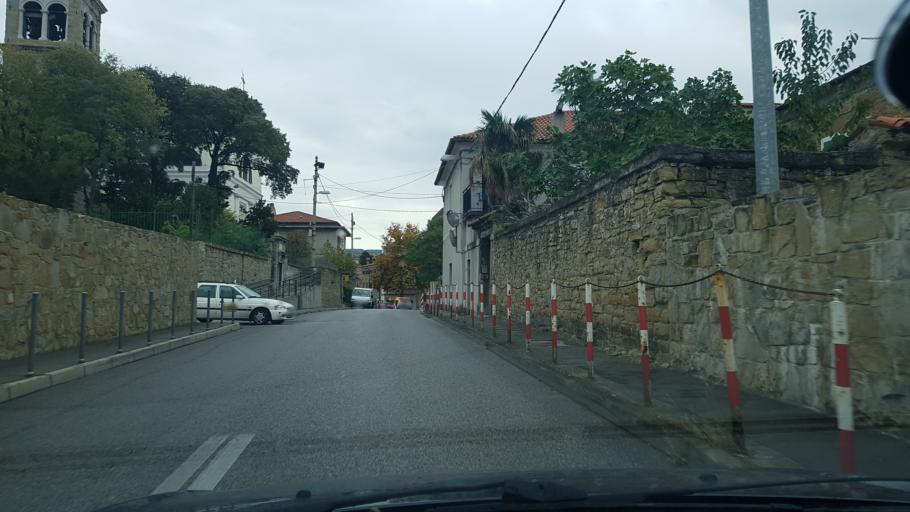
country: IT
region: Friuli Venezia Giulia
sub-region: Provincia di Trieste
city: Trieste
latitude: 45.6254
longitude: 13.7807
